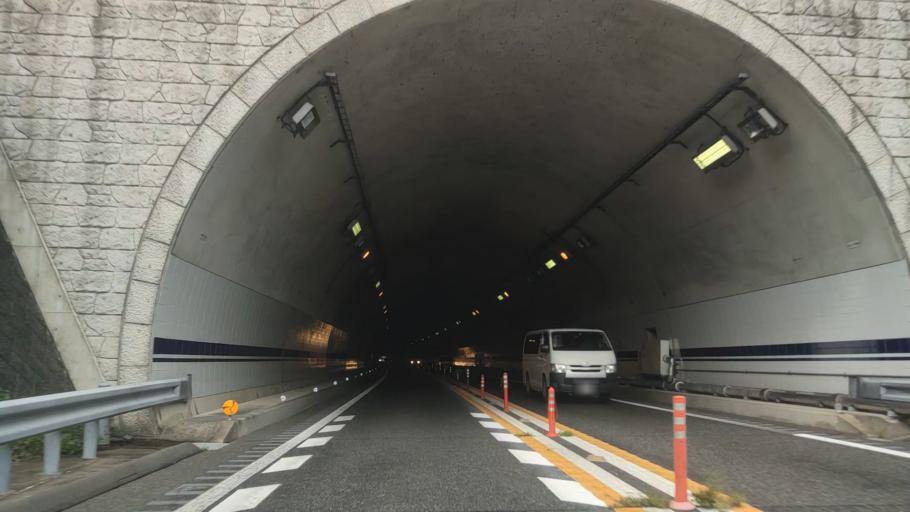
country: JP
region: Wakayama
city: Tanabe
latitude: 33.7675
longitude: 135.3495
